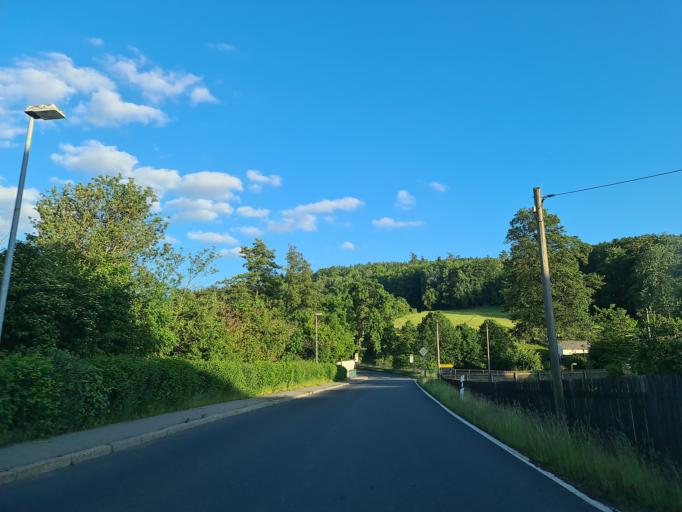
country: DE
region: Saxony
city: Reuth
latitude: 50.4668
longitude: 12.0015
